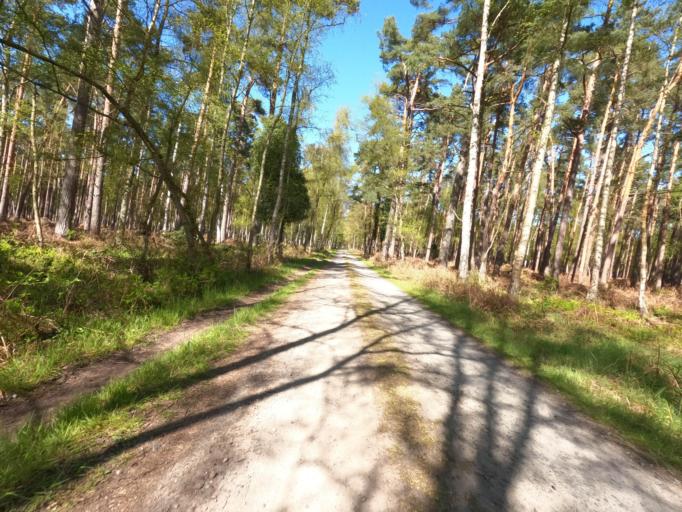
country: DE
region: Mecklenburg-Vorpommern
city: Born
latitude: 54.3982
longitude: 12.5260
